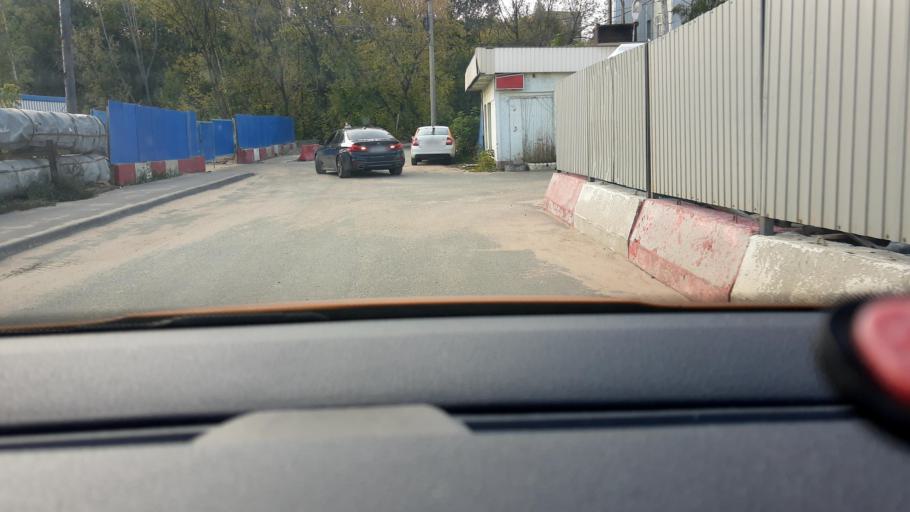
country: RU
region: Moscow
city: Ryazanskiy
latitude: 55.7404
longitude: 37.7300
